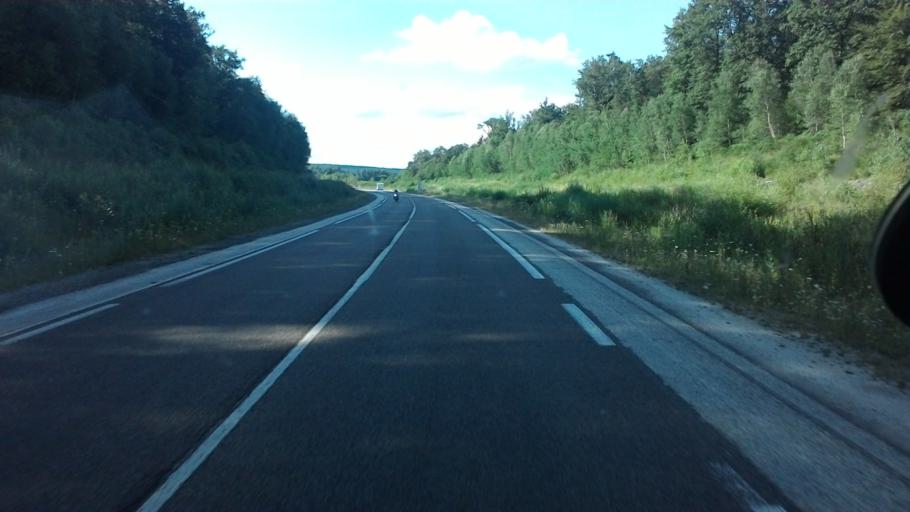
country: FR
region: Franche-Comte
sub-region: Departement de la Haute-Saone
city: Saint-Sauveur
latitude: 47.8041
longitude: 6.4051
